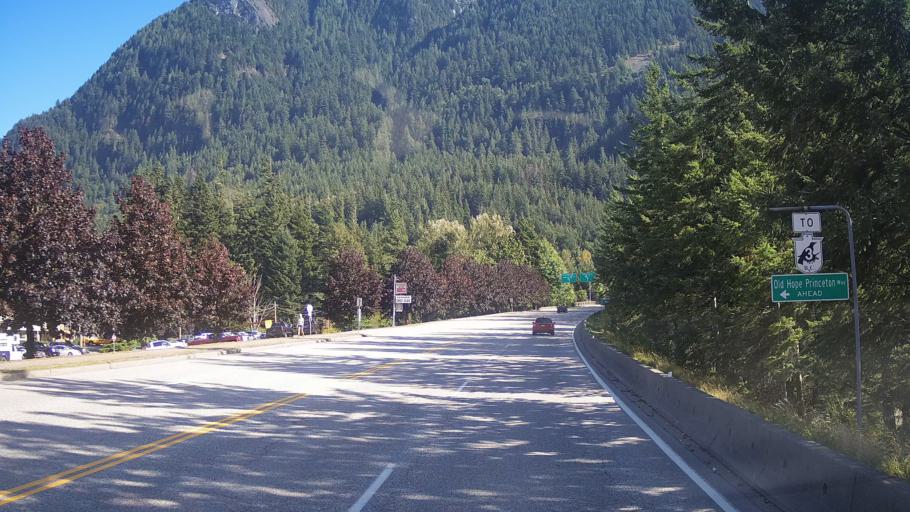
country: CA
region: British Columbia
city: Hope
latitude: 49.3765
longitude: -121.4429
